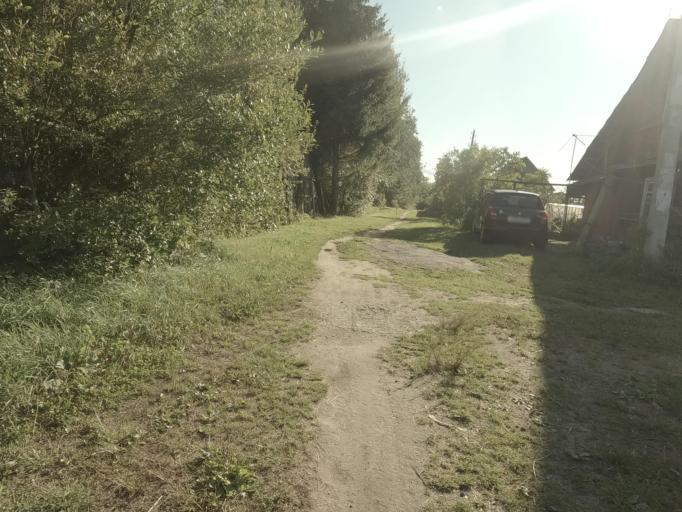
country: RU
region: Leningrad
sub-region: Volosovskiy Rayon
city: Shlissel'burg
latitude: 59.9492
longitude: 31.0145
